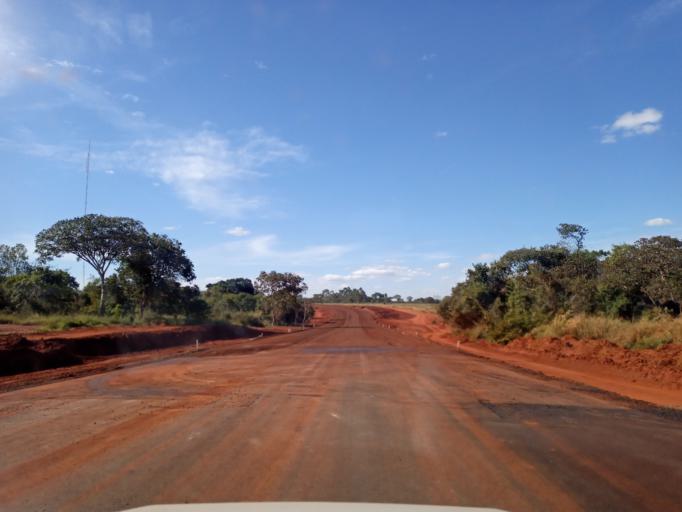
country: BR
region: Minas Gerais
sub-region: Ituiutaba
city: Ituiutaba
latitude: -18.9796
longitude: -49.5074
